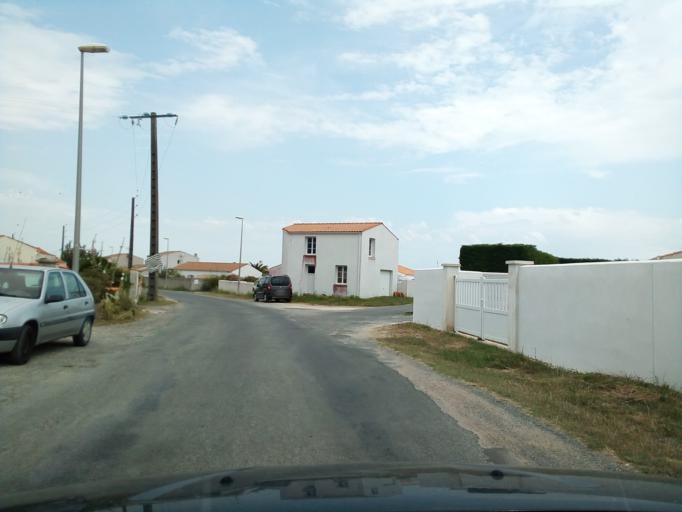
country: FR
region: Poitou-Charentes
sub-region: Departement de la Charente-Maritime
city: Dolus-d'Oleron
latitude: 45.9460
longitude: -1.2977
